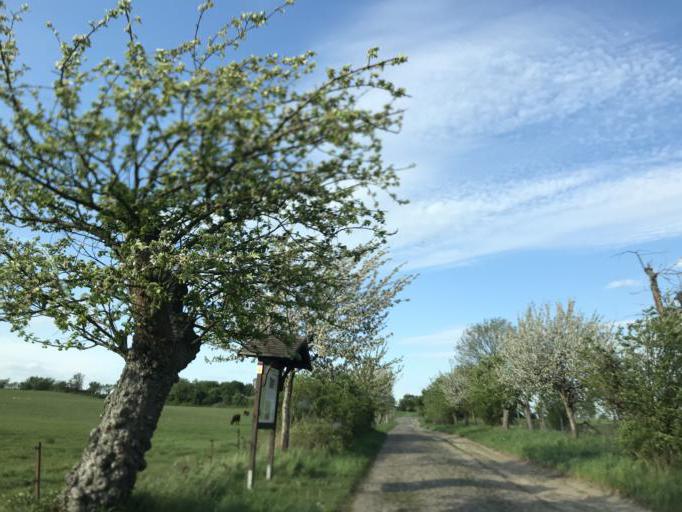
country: DE
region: Brandenburg
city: Joachimsthal
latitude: 52.9742
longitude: 13.7262
